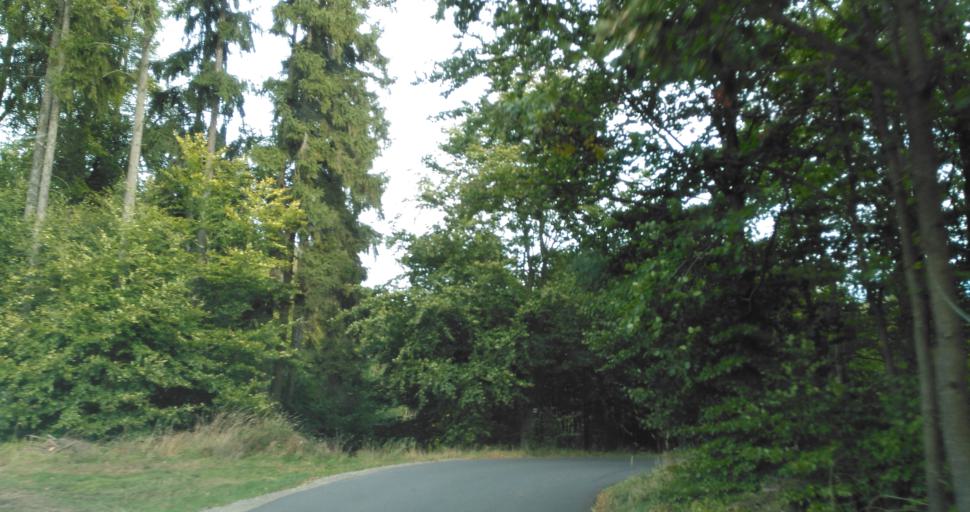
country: CZ
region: Plzensky
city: Zbiroh
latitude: 49.9350
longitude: 13.7774
